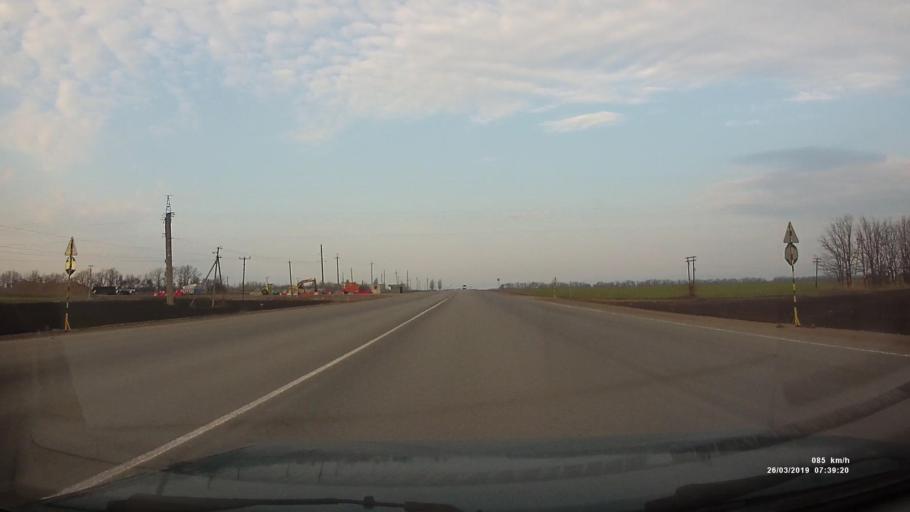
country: RU
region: Rostov
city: Novobessergenovka
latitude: 47.1974
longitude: 38.6672
